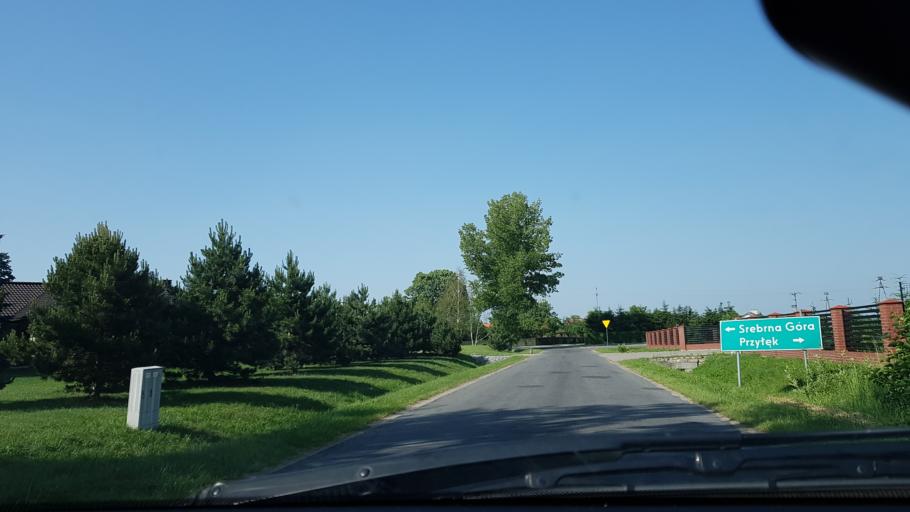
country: PL
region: Lower Silesian Voivodeship
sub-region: Powiat zabkowicki
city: Budzow
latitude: 50.5724
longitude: 16.6800
